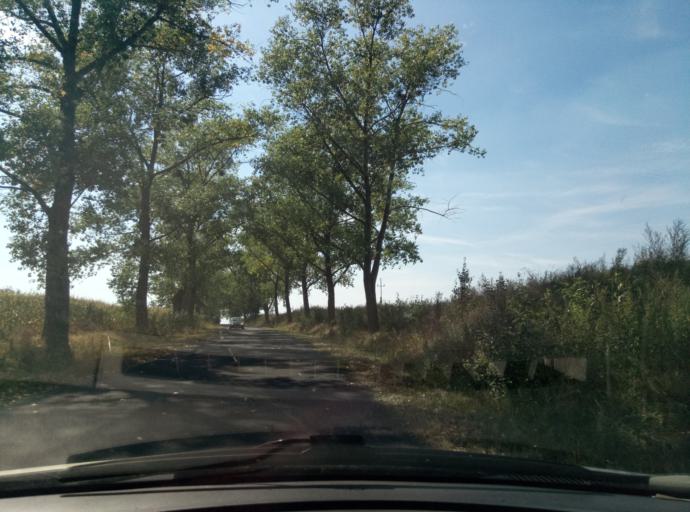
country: PL
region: Kujawsko-Pomorskie
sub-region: Powiat brodnicki
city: Jablonowo Pomorskie
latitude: 53.4014
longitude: 19.2138
